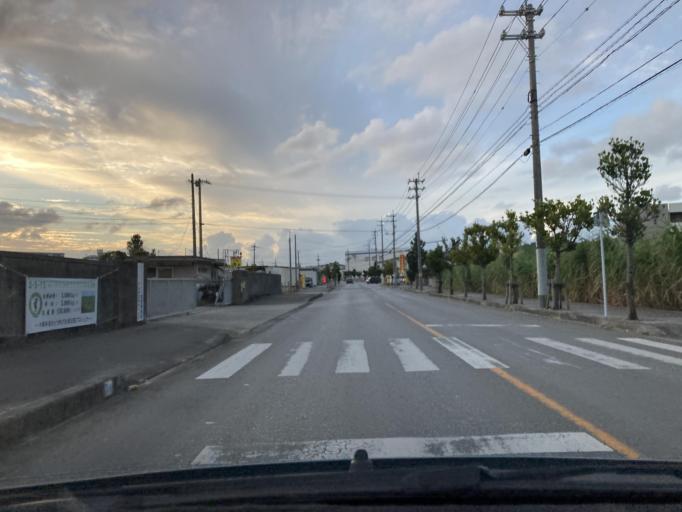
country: JP
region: Okinawa
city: Gushikawa
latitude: 26.3451
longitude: 127.8642
